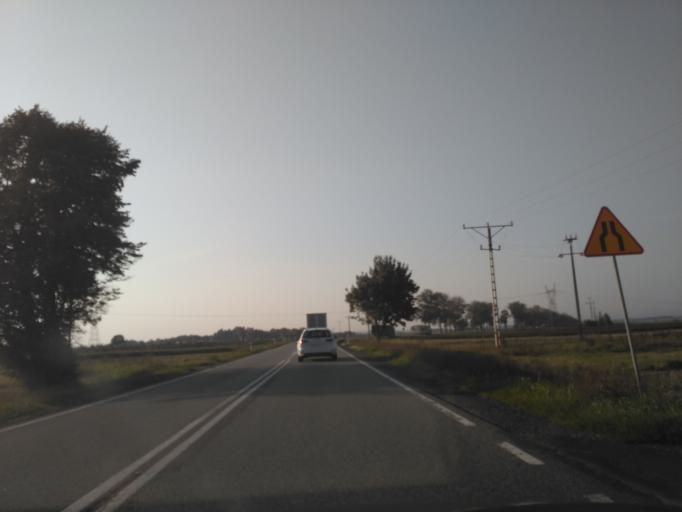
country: PL
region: Lublin Voivodeship
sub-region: Powiat krasnicki
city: Szastarka
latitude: 50.8175
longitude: 22.3179
